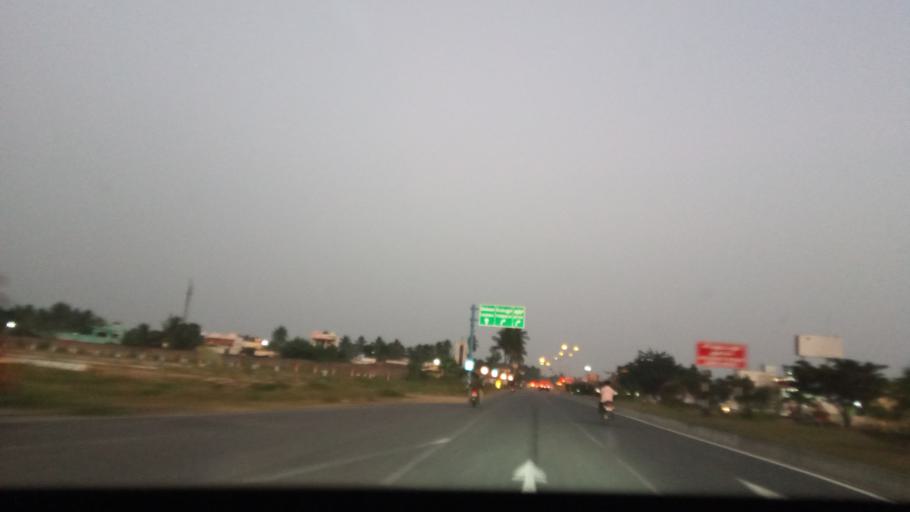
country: IN
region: Tamil Nadu
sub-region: Salem
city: Attur
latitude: 11.6171
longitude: 78.5584
